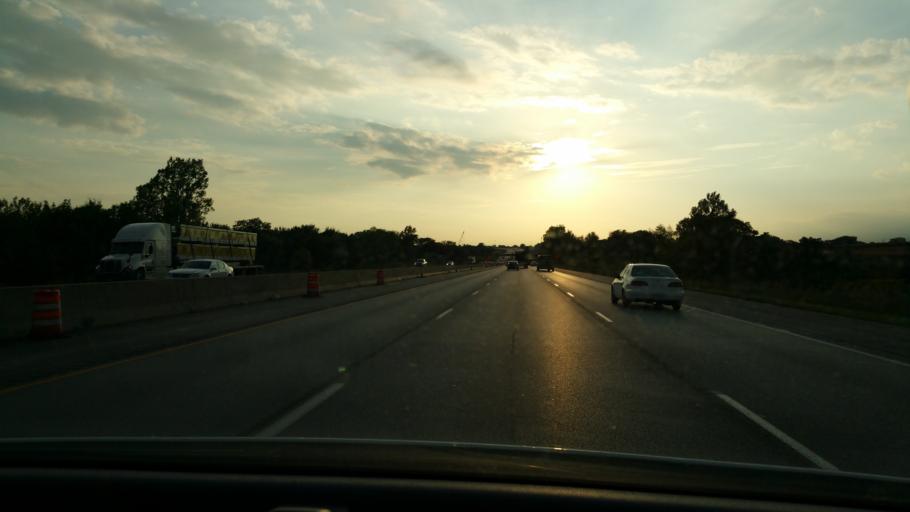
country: US
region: Iowa
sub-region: Polk County
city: Urbandale
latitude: 41.6520
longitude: -93.7456
